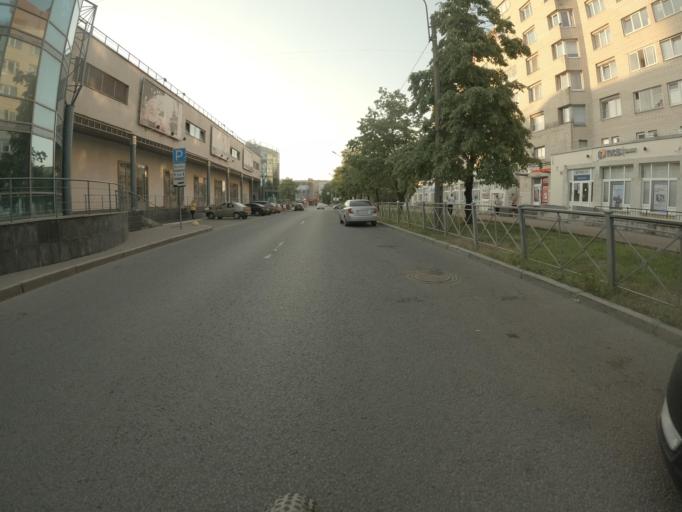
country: RU
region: St.-Petersburg
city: Dachnoye
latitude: 59.8505
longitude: 30.2689
